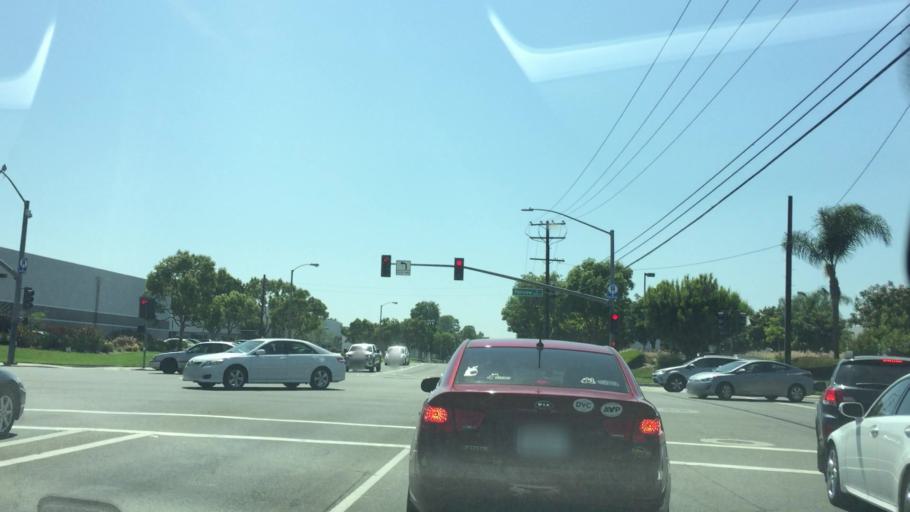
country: US
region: California
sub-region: Orange County
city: Fountain Valley
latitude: 33.7088
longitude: -117.9075
